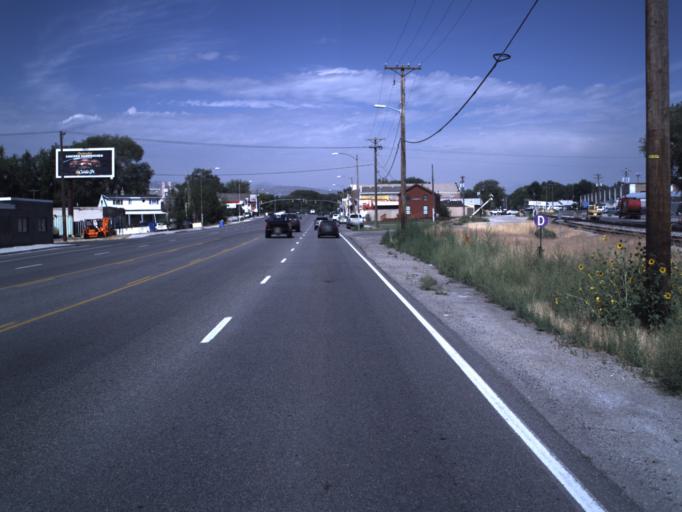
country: US
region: Utah
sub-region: Utah County
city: Lehi
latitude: 40.3955
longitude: -111.8436
